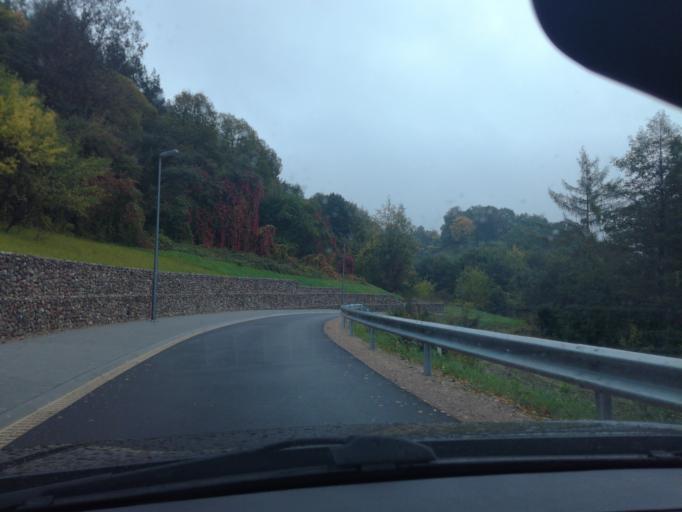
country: LT
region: Alytaus apskritis
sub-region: Alytus
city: Alytus
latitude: 54.3977
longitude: 24.0761
